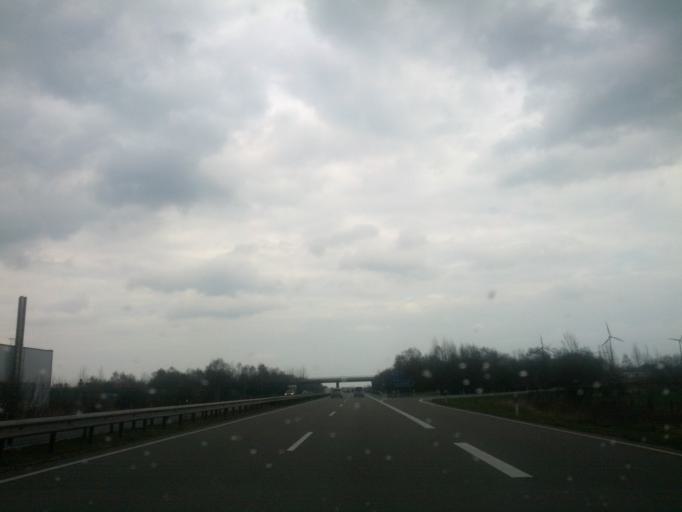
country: DE
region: Lower Saxony
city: Apen
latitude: 53.2584
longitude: 7.7539
